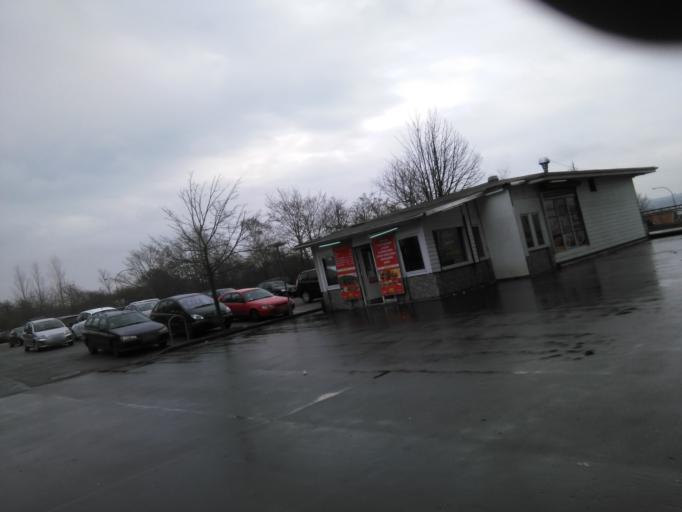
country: DK
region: Central Jutland
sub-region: Arhus Kommune
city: Stavtrup
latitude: 56.1560
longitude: 10.1356
